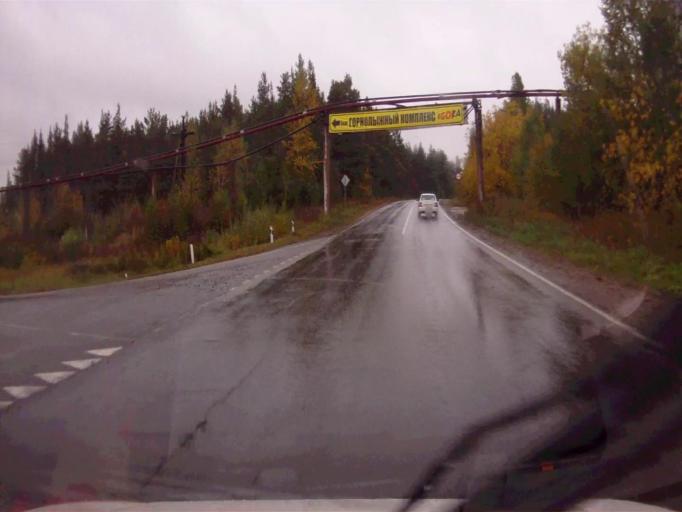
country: RU
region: Chelyabinsk
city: Kyshtym
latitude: 55.7293
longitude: 60.5202
